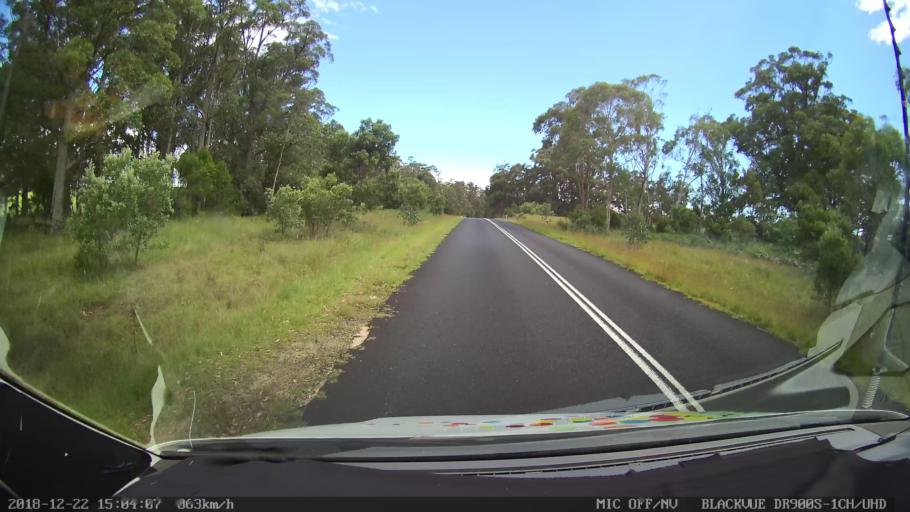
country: AU
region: New South Wales
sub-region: Bellingen
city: Dorrigo
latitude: -30.2716
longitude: 152.4384
